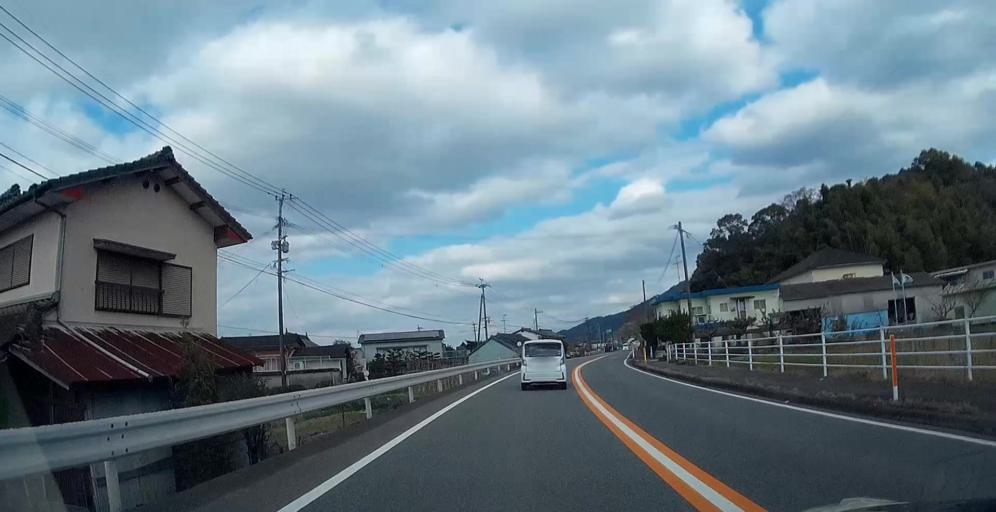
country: JP
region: Kumamoto
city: Yatsushiro
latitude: 32.4470
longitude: 130.5874
